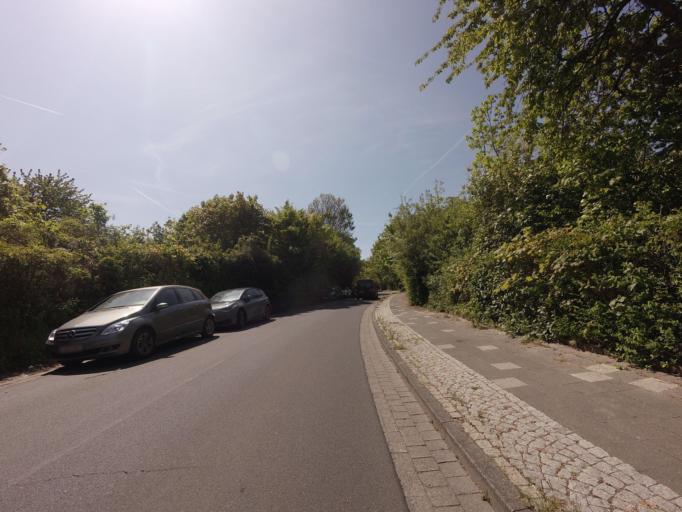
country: DE
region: Lower Saxony
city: Hildesheim
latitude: 52.1478
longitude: 9.9738
